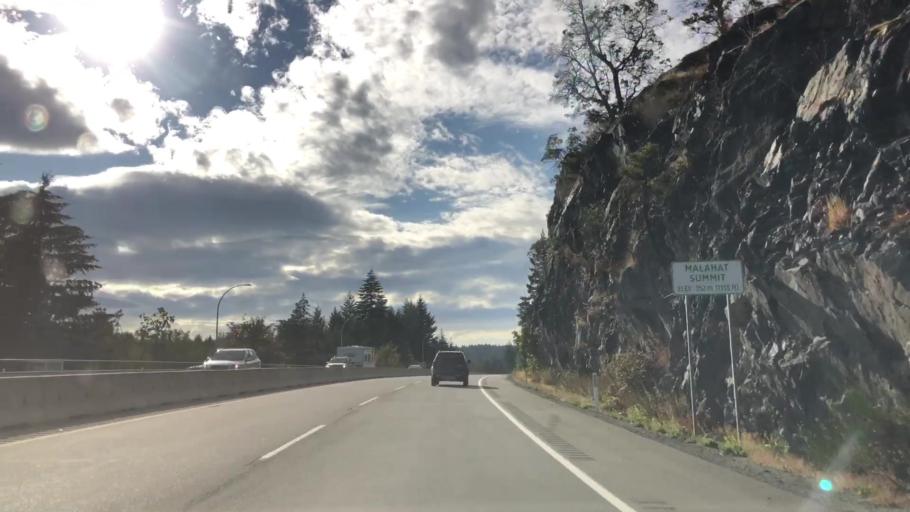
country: CA
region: British Columbia
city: Langford
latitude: 48.5676
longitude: -123.5466
